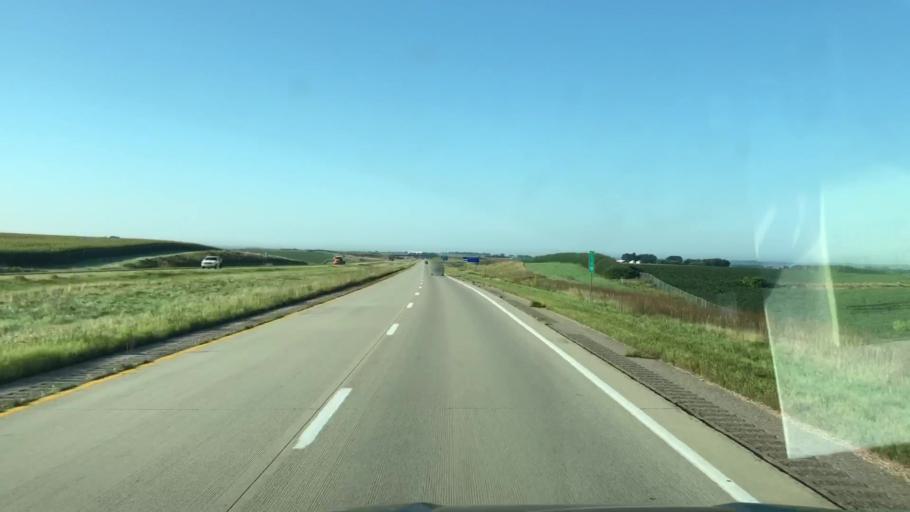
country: US
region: Iowa
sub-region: Plymouth County
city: Le Mars
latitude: 42.8056
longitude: -96.1994
